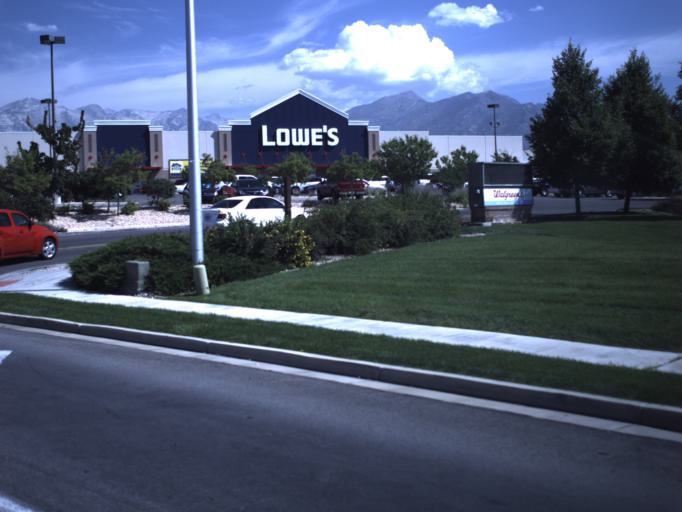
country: US
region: Utah
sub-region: Utah County
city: Lehi
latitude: 40.3894
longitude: -111.8267
